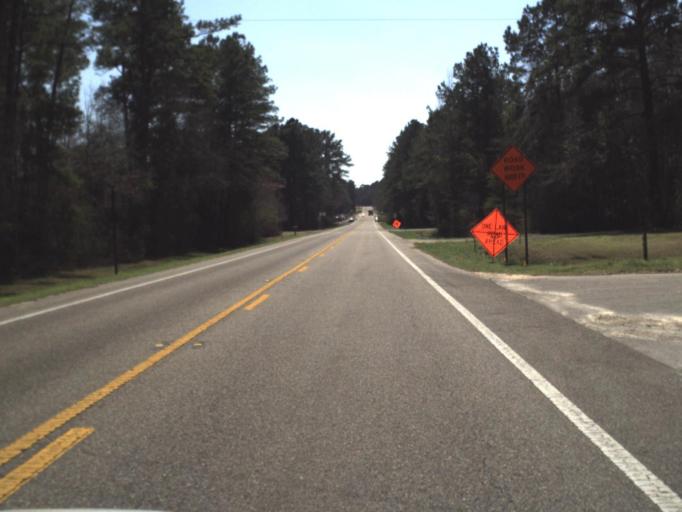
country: US
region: Florida
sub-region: Calhoun County
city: Blountstown
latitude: 30.5345
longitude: -85.0288
